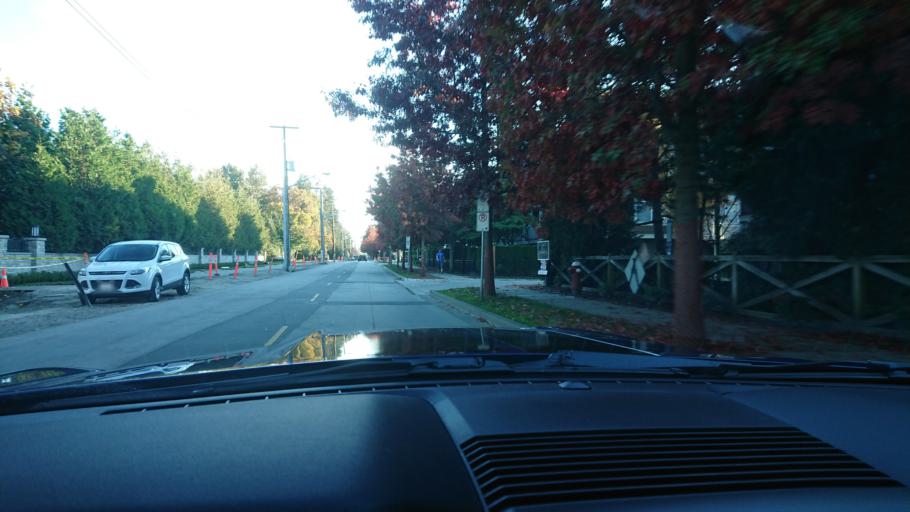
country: CA
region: British Columbia
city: Richmond
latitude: 49.1243
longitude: -123.1589
